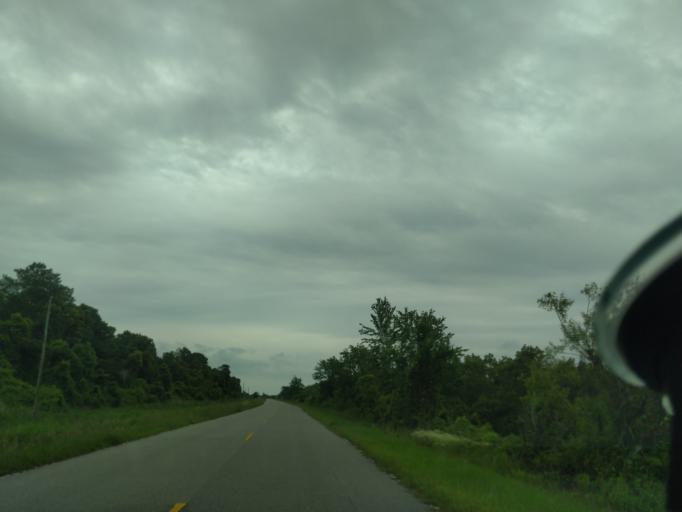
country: US
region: North Carolina
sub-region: Beaufort County
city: Belhaven
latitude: 35.7477
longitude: -76.5001
